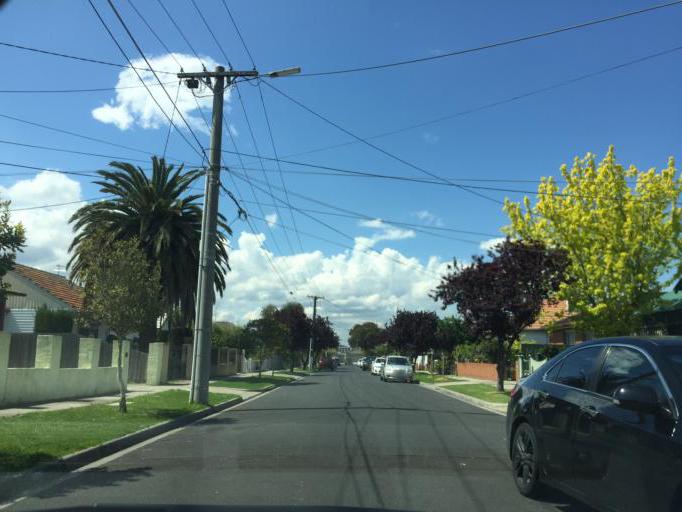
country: AU
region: Victoria
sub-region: Maribyrnong
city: Maribyrnong
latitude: -37.7878
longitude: 144.8771
